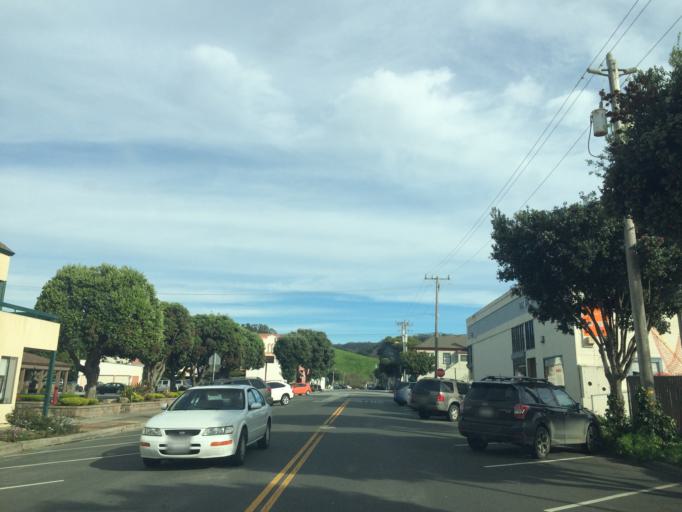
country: US
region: California
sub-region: San Mateo County
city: Half Moon Bay
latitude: 37.4638
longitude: -122.4309
